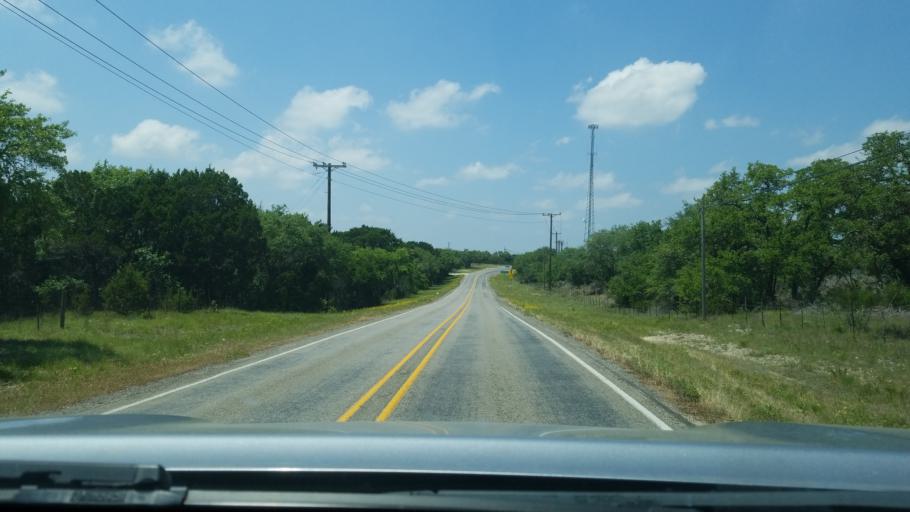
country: US
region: Texas
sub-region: Hays County
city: Woodcreek
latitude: 30.0460
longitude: -98.1964
